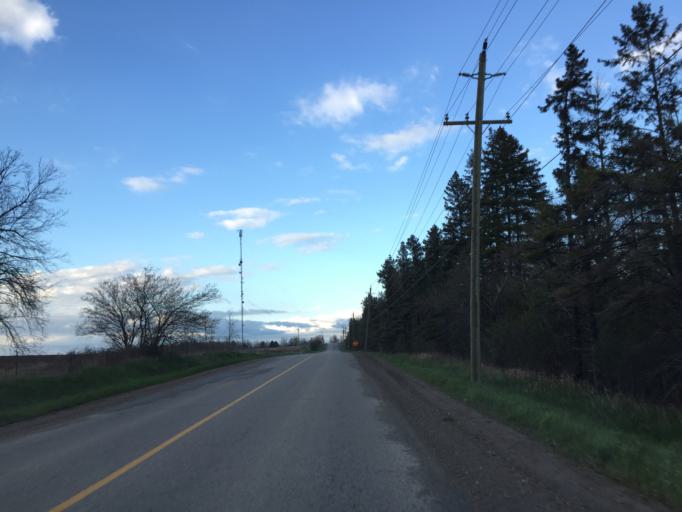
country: CA
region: Ontario
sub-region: Wellington County
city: Guelph
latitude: 43.5930
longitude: -80.2895
